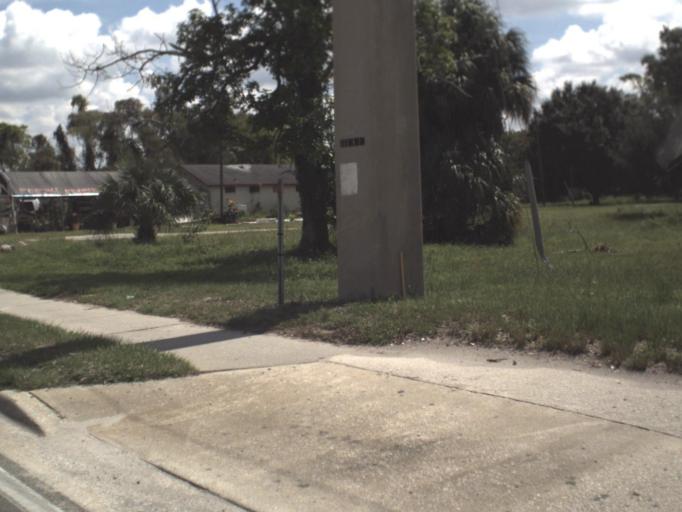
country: US
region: Florida
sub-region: Manatee County
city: South Bradenton
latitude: 27.4623
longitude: -82.5802
